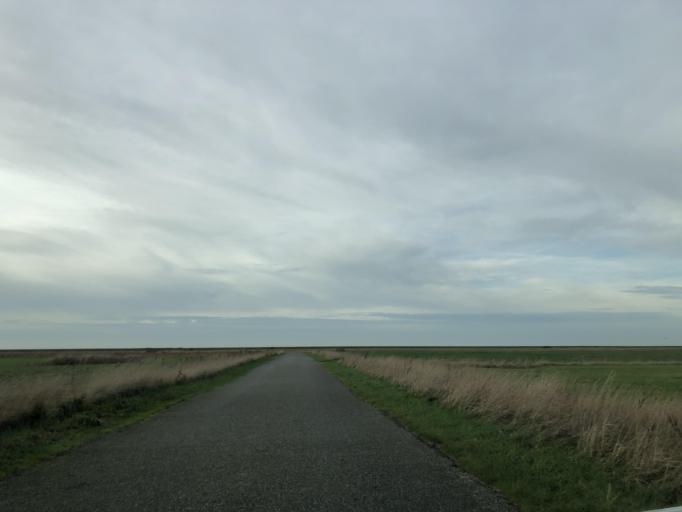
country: DK
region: South Denmark
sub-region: Tonder Kommune
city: Sherrebek
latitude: 55.1923
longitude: 8.7013
